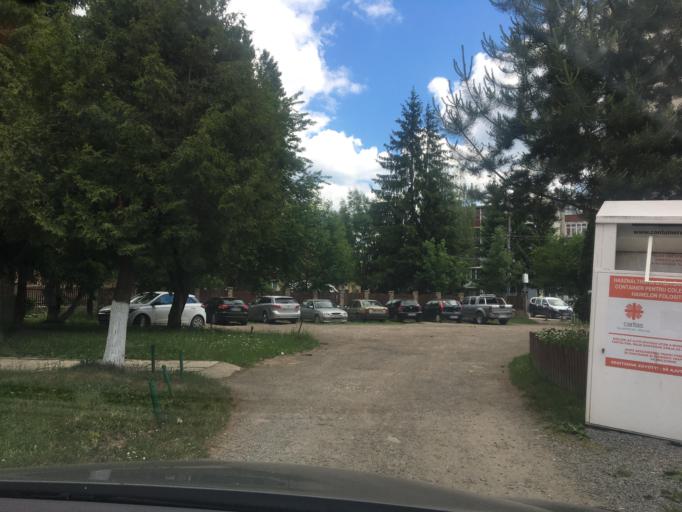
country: RO
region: Harghita
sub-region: Municipiul Gheorgheni
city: Gheorgheni
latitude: 46.7249
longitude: 25.6039
